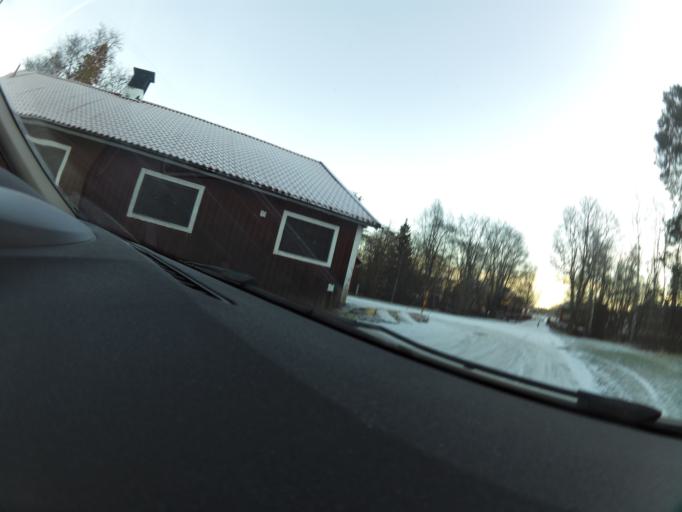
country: SE
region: Gaevleborg
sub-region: Gavle Kommun
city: Gavle
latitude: 60.6691
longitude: 17.1117
